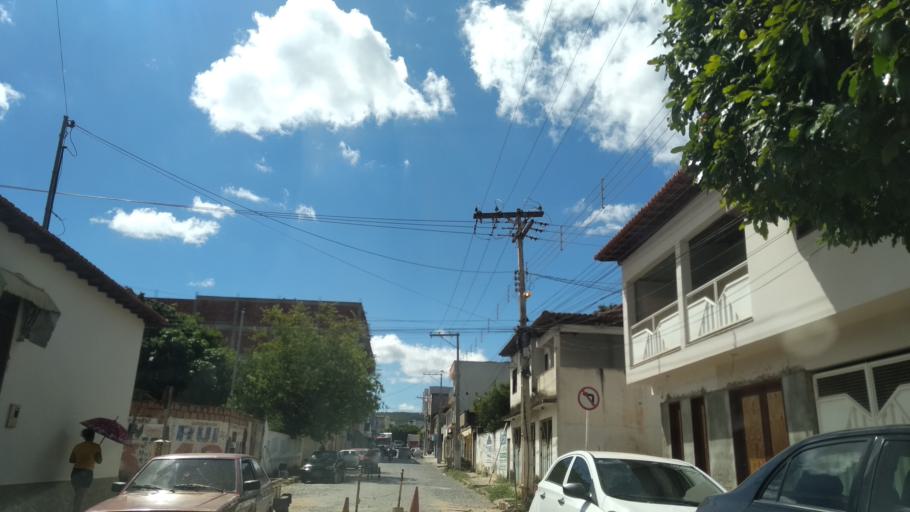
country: BR
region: Bahia
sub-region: Caetite
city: Caetite
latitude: -14.0661
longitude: -42.4882
